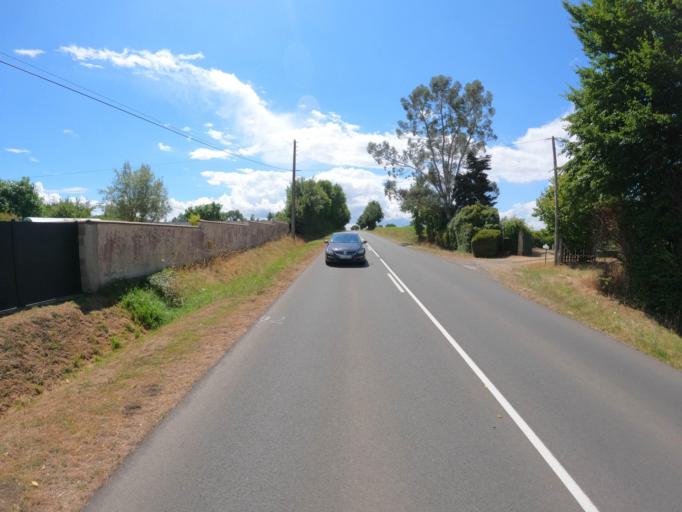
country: FR
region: Pays de la Loire
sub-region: Departement de Maine-et-Loire
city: Champigne
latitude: 47.6525
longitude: -0.5757
